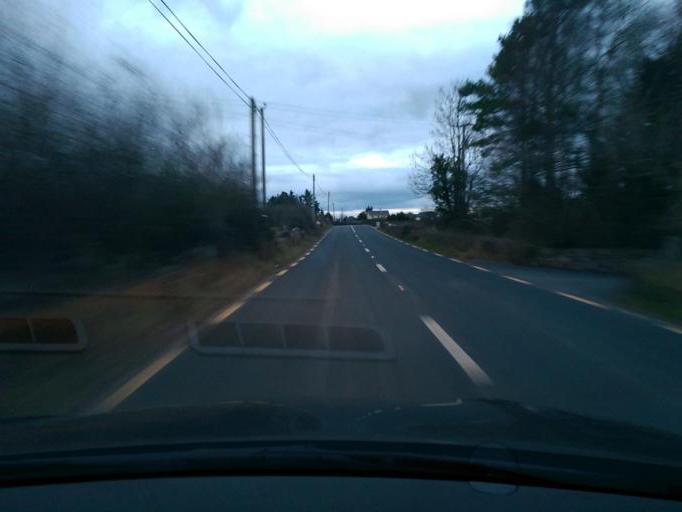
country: IE
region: Connaught
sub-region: County Galway
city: Portumna
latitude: 53.1176
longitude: -8.2395
